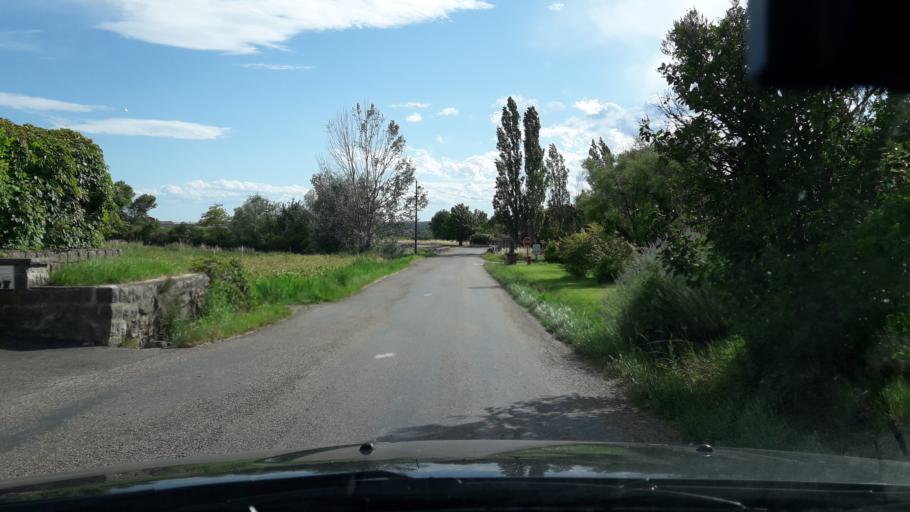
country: FR
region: Rhone-Alpes
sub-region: Departement de l'Ardeche
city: Vesseaux
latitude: 44.6182
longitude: 4.4758
